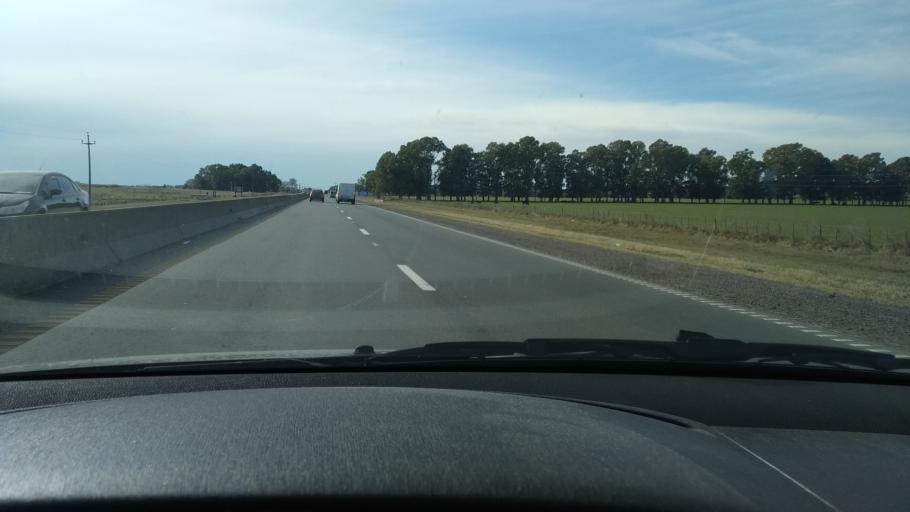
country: AR
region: Buenos Aires
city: Olavarria
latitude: -36.9218
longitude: -60.2112
